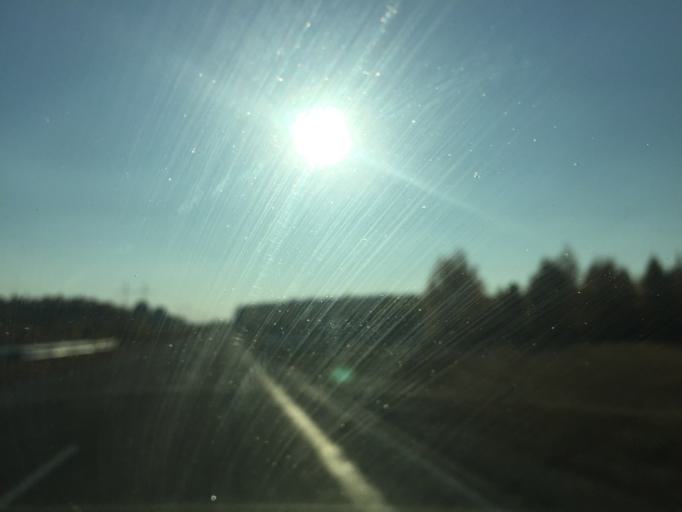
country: BY
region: Gomel
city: Dobrush
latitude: 52.3692
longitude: 31.2520
